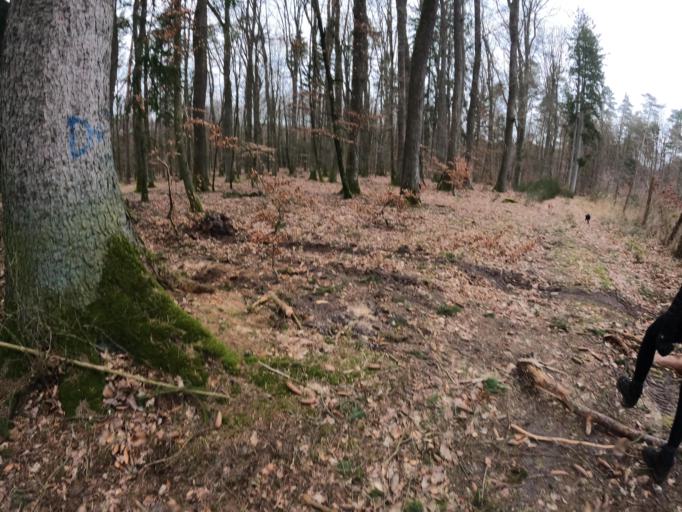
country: PL
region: West Pomeranian Voivodeship
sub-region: Powiat kamienski
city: Golczewo
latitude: 53.8137
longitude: 15.0237
